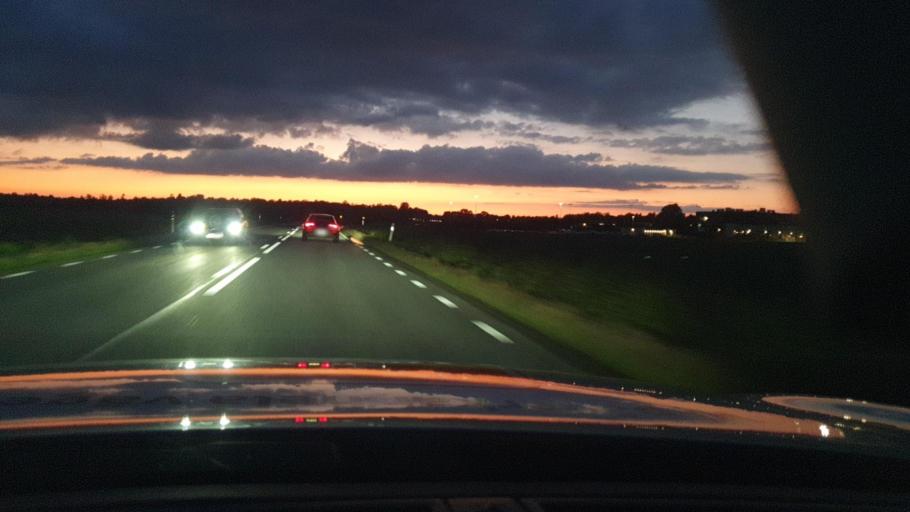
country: SE
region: Skane
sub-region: Angelholms Kommun
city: AEngelholm
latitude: 56.2234
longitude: 12.8529
